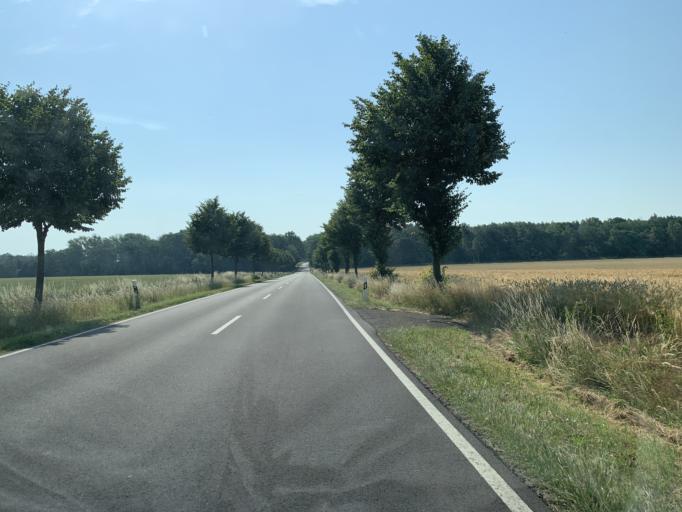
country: DE
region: Saxony-Anhalt
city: Erxleben
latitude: 52.2361
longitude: 11.2168
